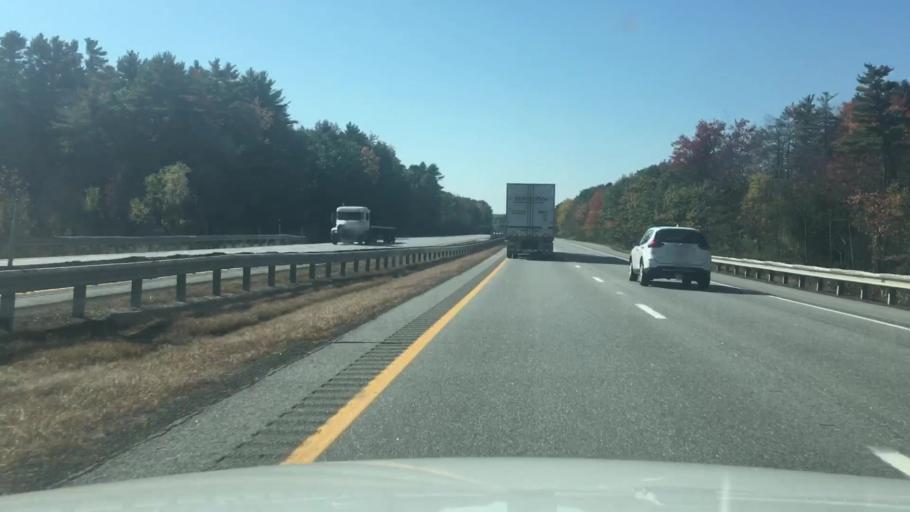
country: US
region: Maine
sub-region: Cumberland County
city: Falmouth
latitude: 43.7312
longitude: -70.2696
